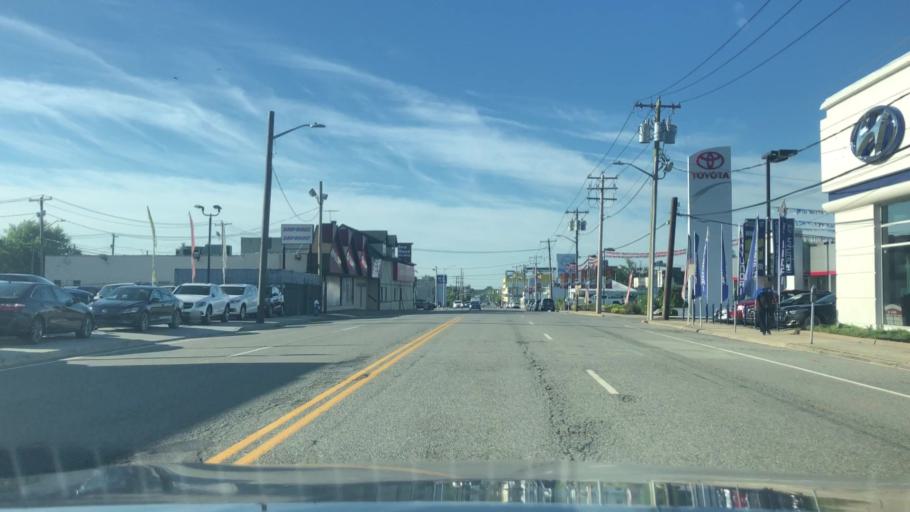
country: US
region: New York
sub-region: Nassau County
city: Garden City
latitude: 40.7155
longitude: -73.6302
